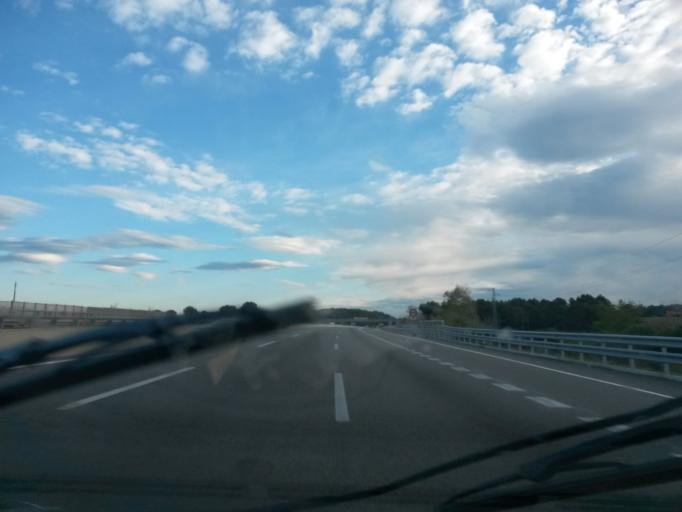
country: ES
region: Catalonia
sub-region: Provincia de Girona
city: Vilademuls
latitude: 42.1265
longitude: 2.9121
